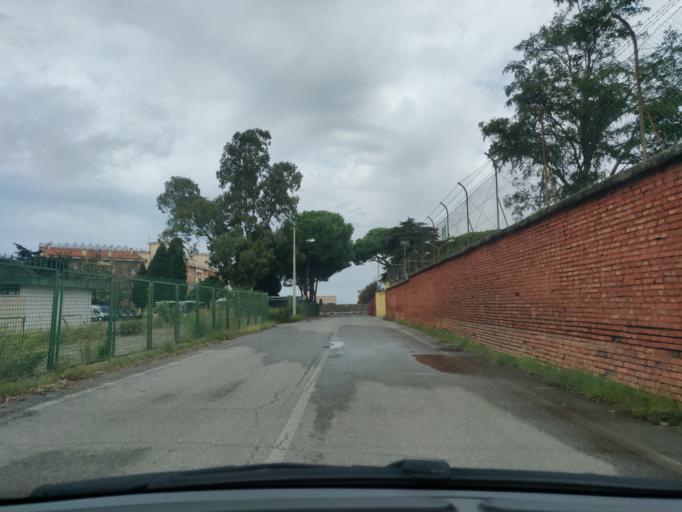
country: IT
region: Latium
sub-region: Citta metropolitana di Roma Capitale
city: Aurelia
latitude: 42.1399
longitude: 11.7863
